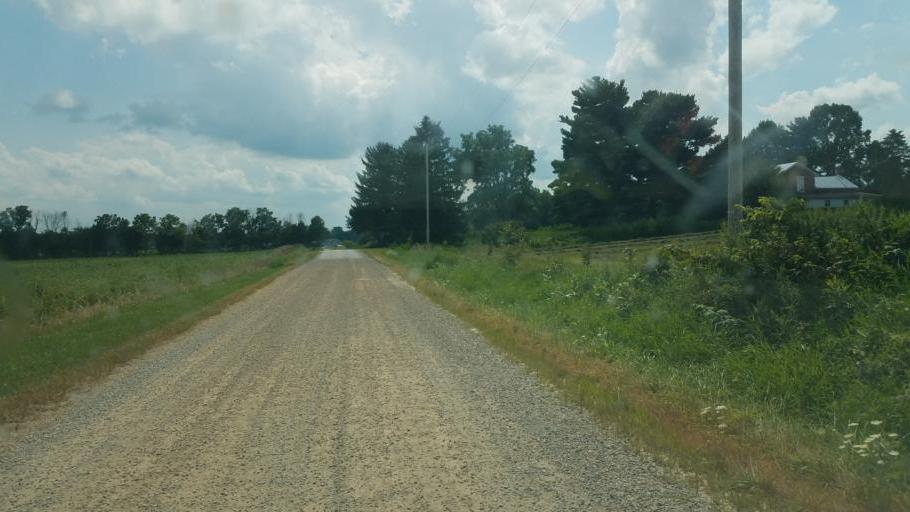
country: US
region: Ohio
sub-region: Knox County
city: Centerburg
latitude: 40.3244
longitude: -82.5939
